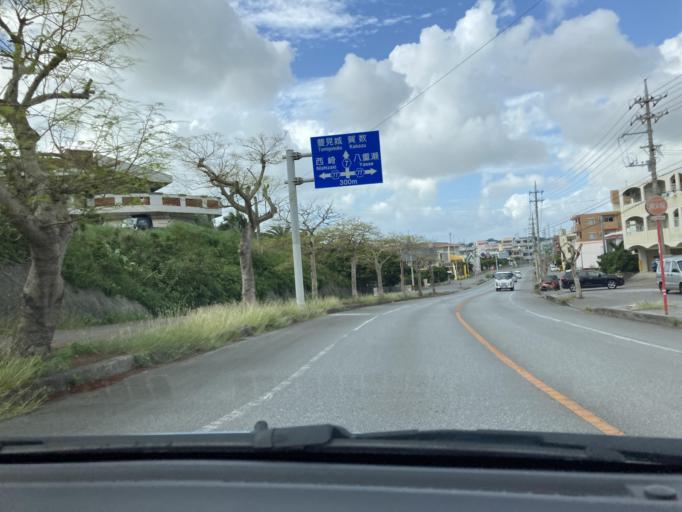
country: JP
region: Okinawa
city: Itoman
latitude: 26.1310
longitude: 127.6875
